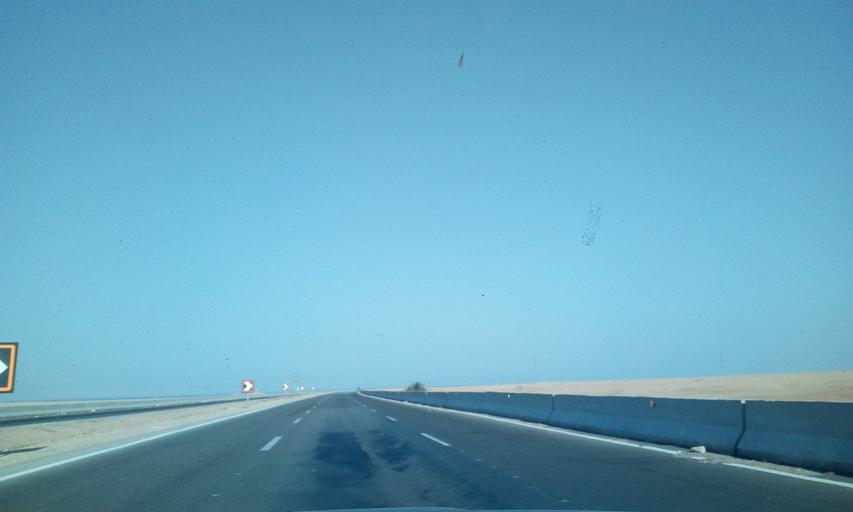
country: EG
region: As Suways
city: Ain Sukhna
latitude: 29.1102
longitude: 32.5857
